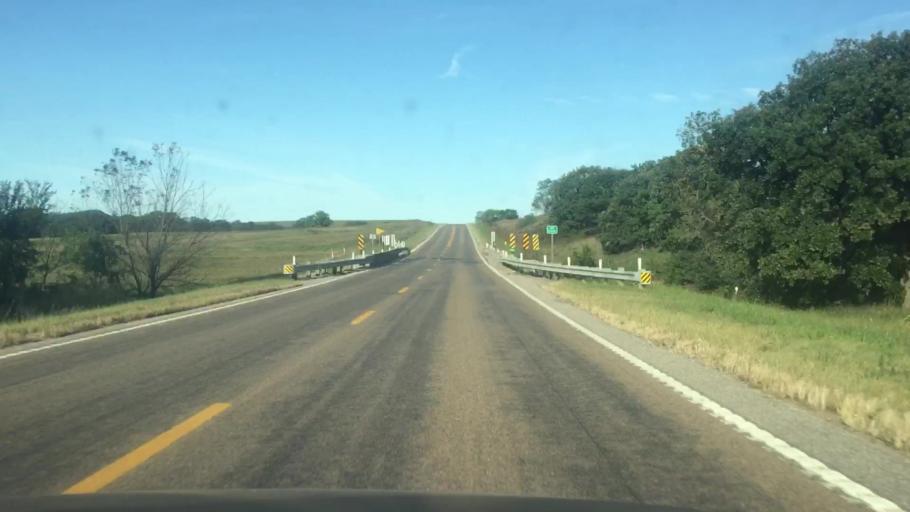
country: US
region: Nebraska
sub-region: Thayer County
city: Hebron
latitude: 40.1473
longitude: -97.5208
